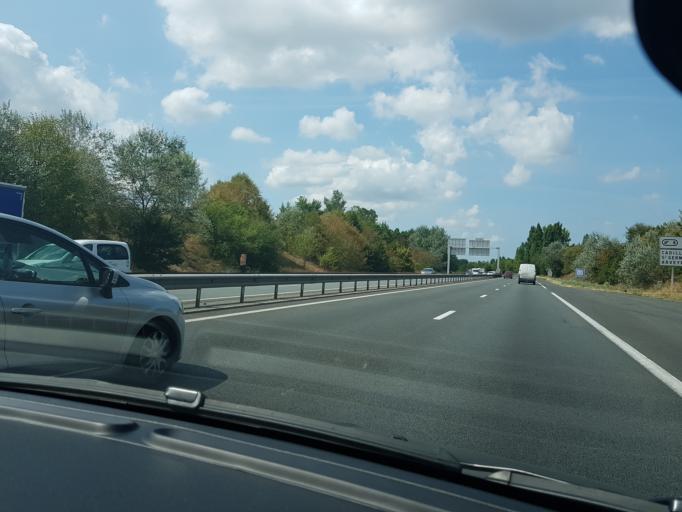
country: FR
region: Aquitaine
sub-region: Departement de la Gironde
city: Arveyres
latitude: 44.8776
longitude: -0.2931
